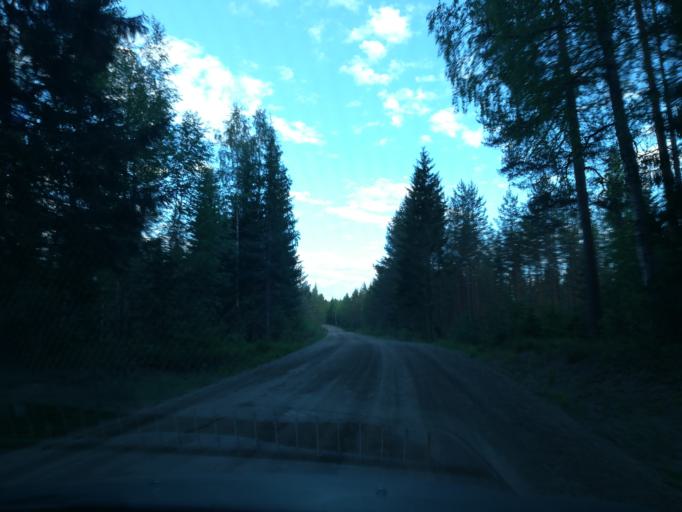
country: FI
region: Southern Savonia
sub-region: Mikkeli
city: Puumala
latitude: 61.6251
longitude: 28.1083
